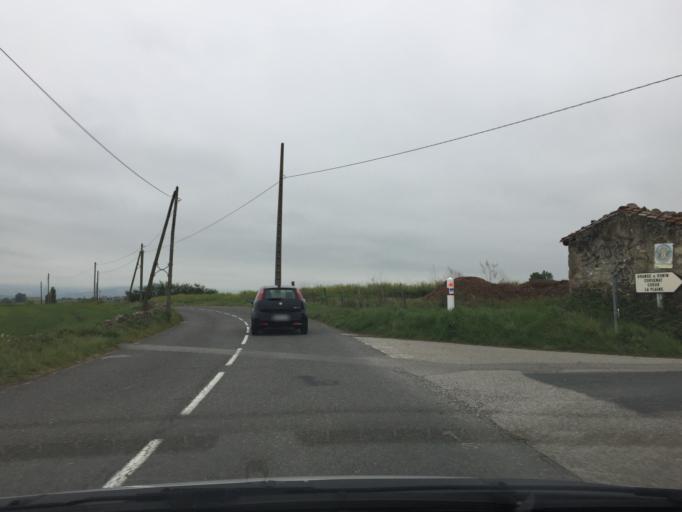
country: FR
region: Rhone-Alpes
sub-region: Departement du Rhone
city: Mornant
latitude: 45.6070
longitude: 4.6677
